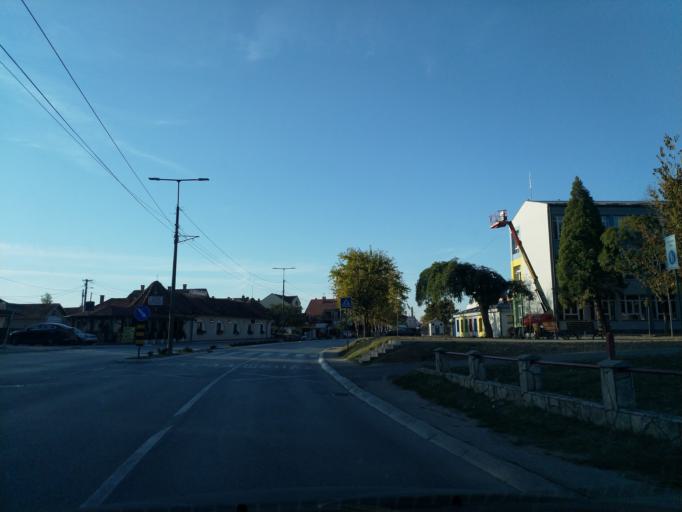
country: RS
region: Central Serbia
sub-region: Pomoravski Okrug
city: Svilajnac
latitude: 44.2302
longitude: 21.1934
